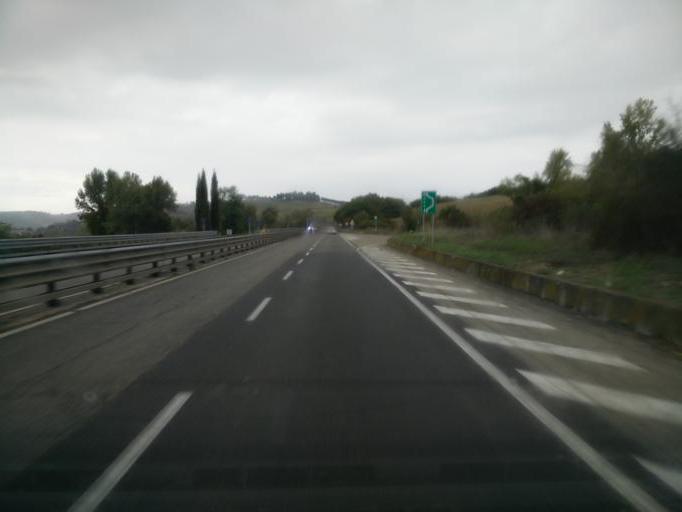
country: IT
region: Tuscany
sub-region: Provincia di Siena
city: Belverde
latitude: 43.3737
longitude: 11.2867
